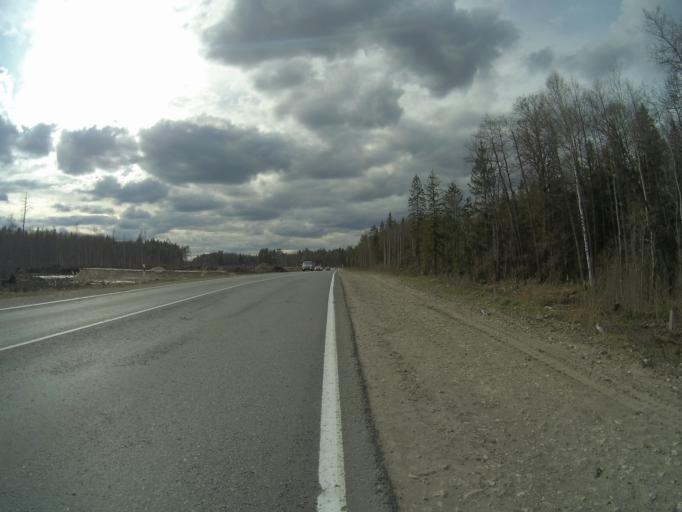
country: RU
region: Vladimir
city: Orgtrud
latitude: 56.0110
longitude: 40.6066
